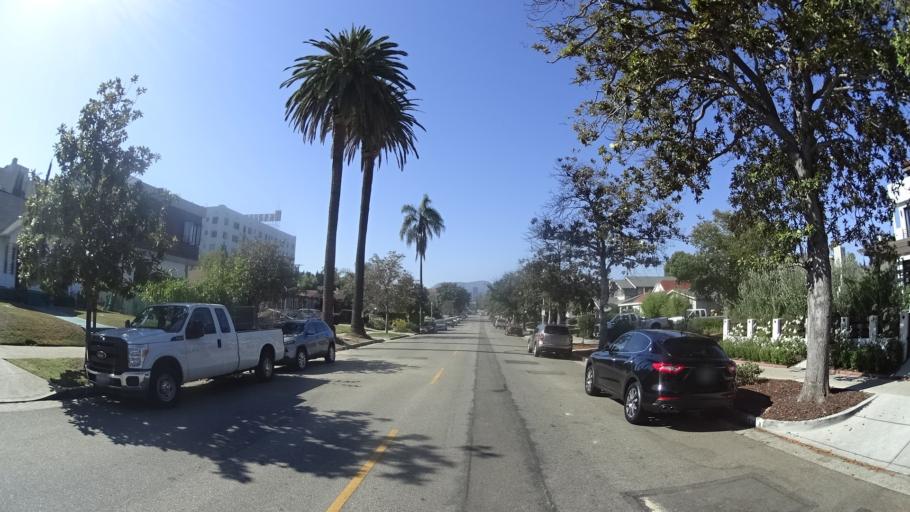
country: US
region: California
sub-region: Los Angeles County
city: Hollywood
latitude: 34.0800
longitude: -118.3260
